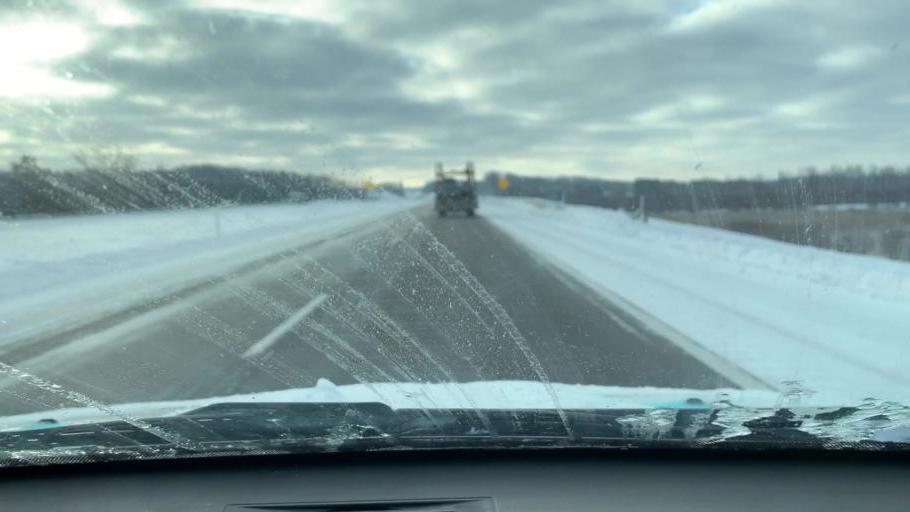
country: US
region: Michigan
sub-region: Wexford County
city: Manton
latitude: 44.4311
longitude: -85.3903
